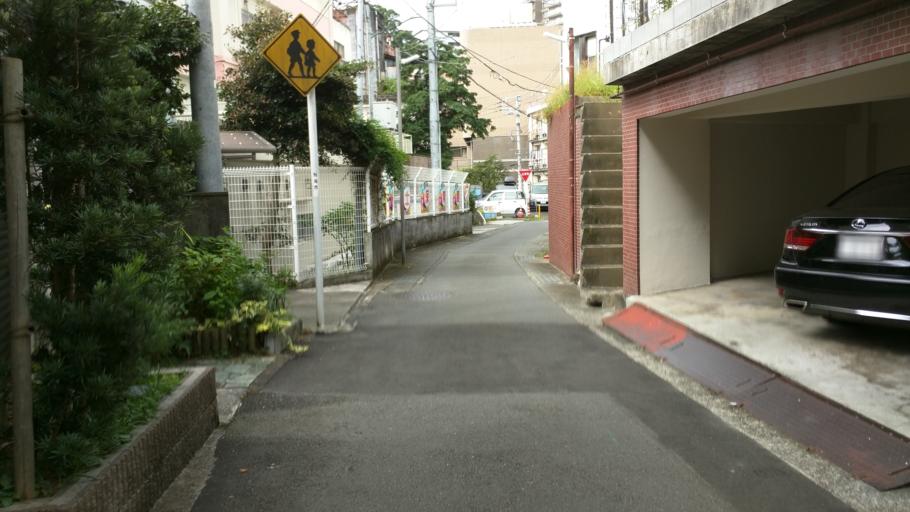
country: JP
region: Shizuoka
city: Atami
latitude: 35.1010
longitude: 139.0761
